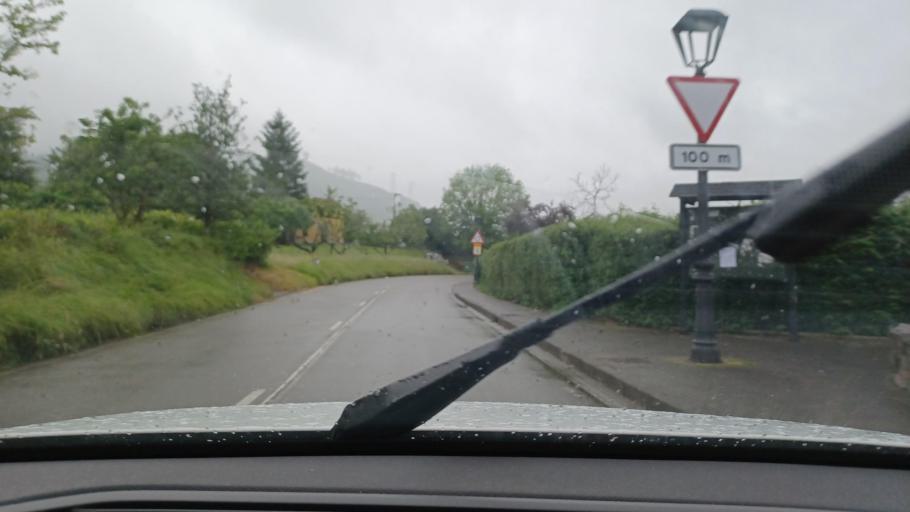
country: ES
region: Asturias
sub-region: Province of Asturias
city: Castandiello
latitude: 43.3113
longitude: -5.8793
